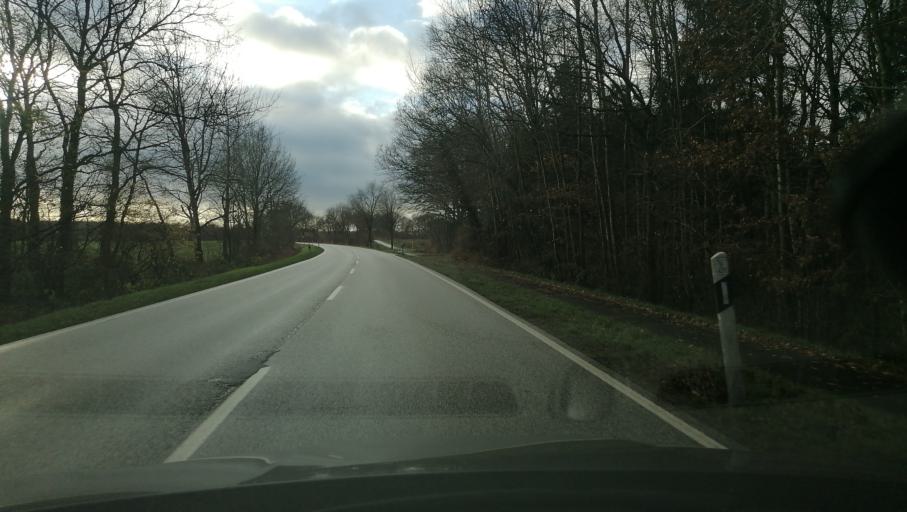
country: DE
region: Schleswig-Holstein
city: Sarzbuttel
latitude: 54.1101
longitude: 9.2020
